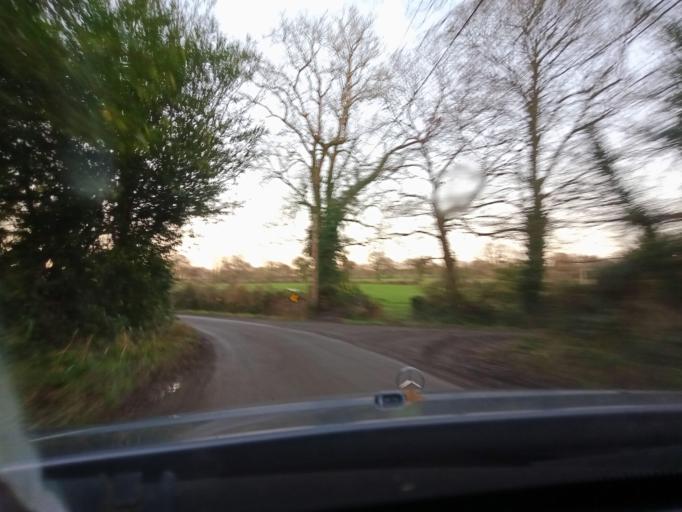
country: IE
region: Leinster
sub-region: Kilkenny
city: Thomastown
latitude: 52.4584
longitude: -7.1025
